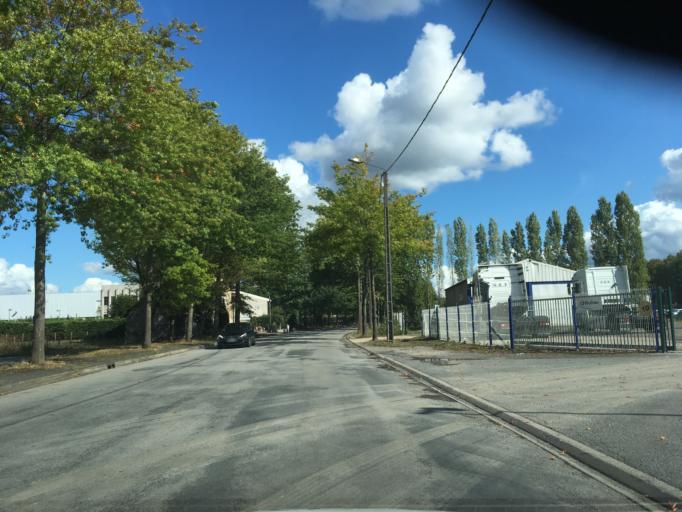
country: FR
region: Limousin
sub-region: Departement de la Correze
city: Saint-Pantaleon-de-Larche
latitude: 45.1567
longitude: 1.4749
